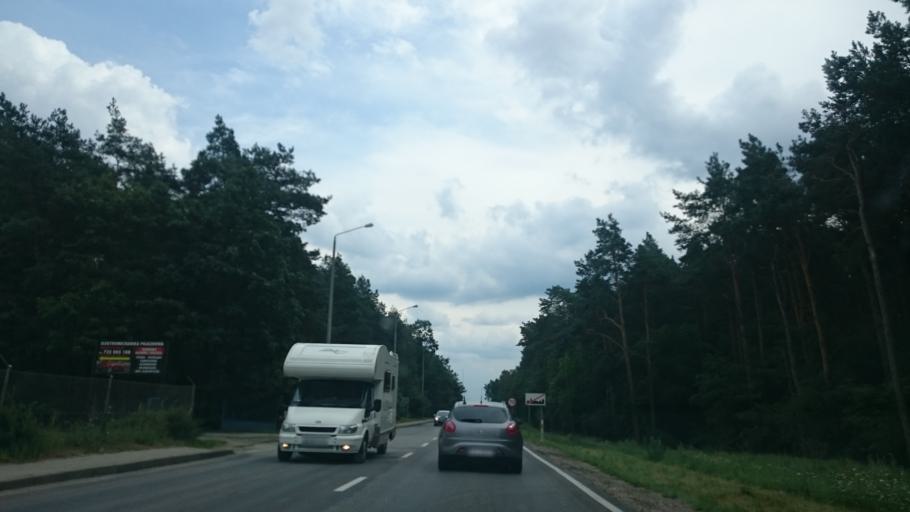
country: PL
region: Kujawsko-Pomorskie
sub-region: Powiat tucholski
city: Tuchola
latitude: 53.5768
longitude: 17.8799
